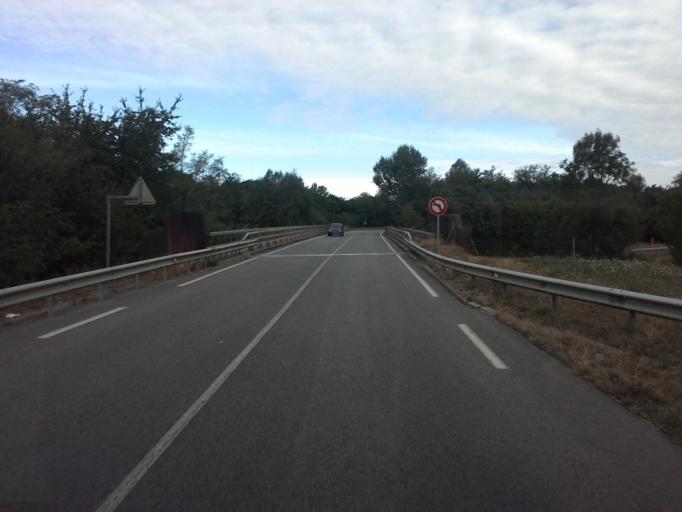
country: FR
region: Rhone-Alpes
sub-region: Departement de l'Ain
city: Saint-Martin-du-Mont
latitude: 46.0670
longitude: 5.3285
